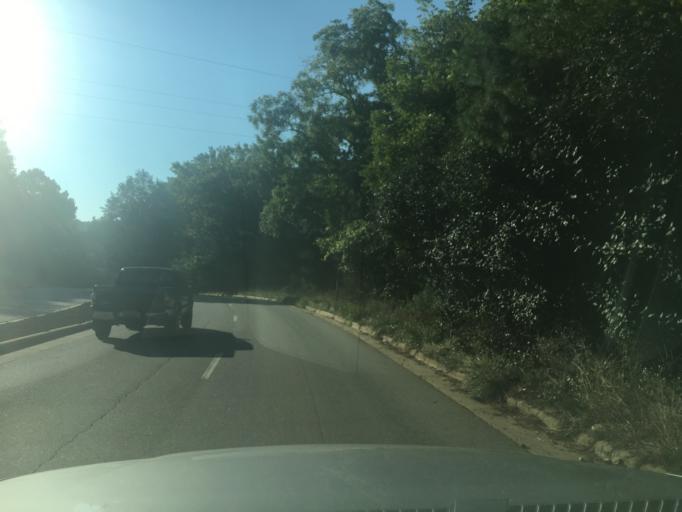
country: US
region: North Carolina
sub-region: Buncombe County
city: Asheville
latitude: 35.6121
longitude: -82.5668
